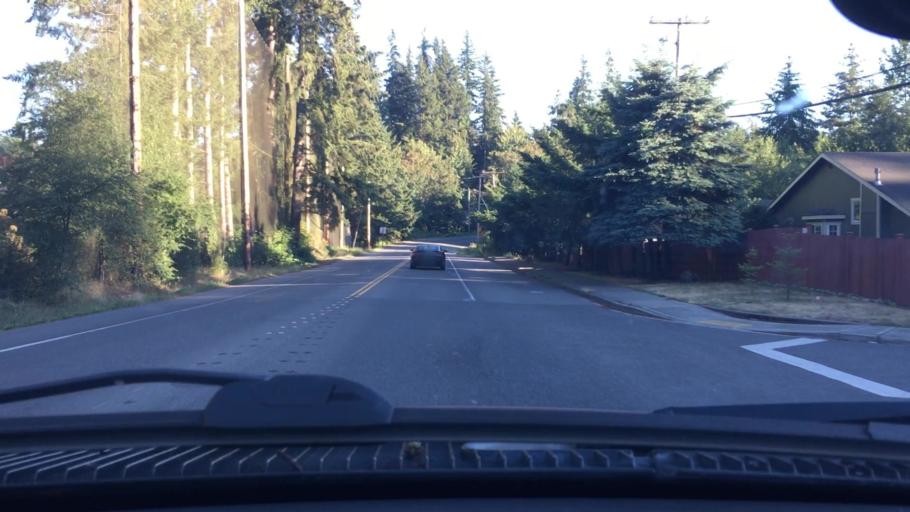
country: US
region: Washington
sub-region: King County
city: Maple Valley
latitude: 47.3783
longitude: -122.0482
